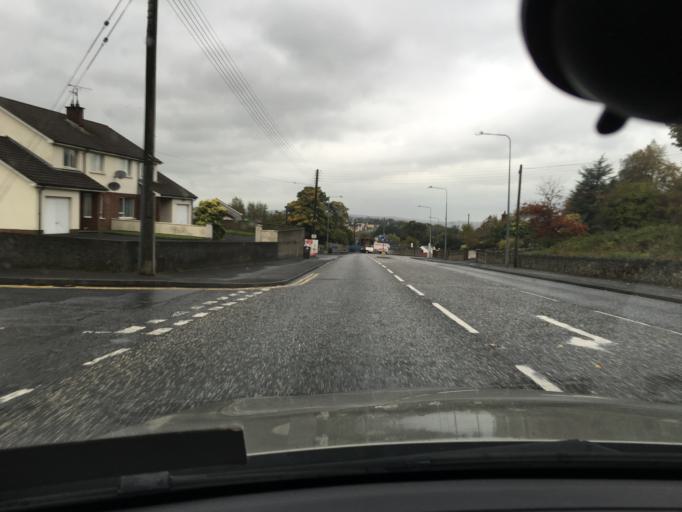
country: GB
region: Northern Ireland
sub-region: Newry and Mourne District
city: Newry
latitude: 54.1533
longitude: -6.3462
